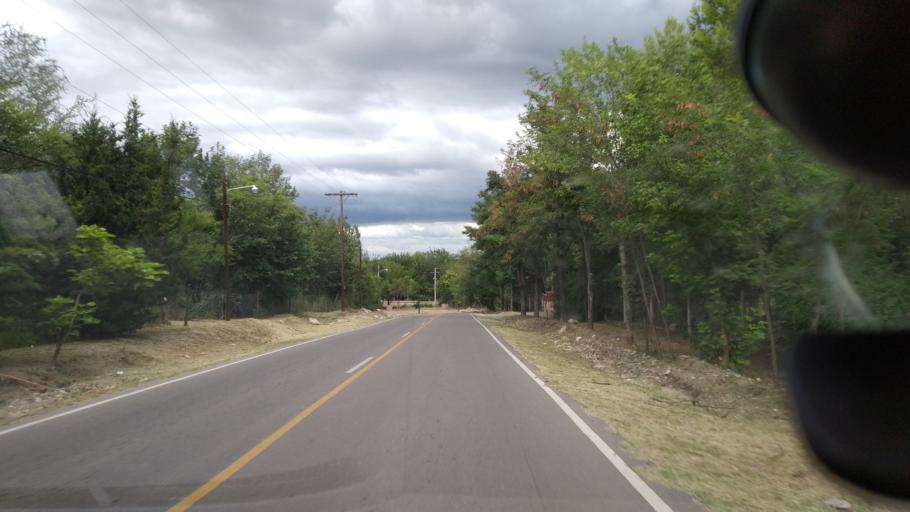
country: AR
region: Cordoba
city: Villa Las Rosas
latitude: -31.9373
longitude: -65.0398
